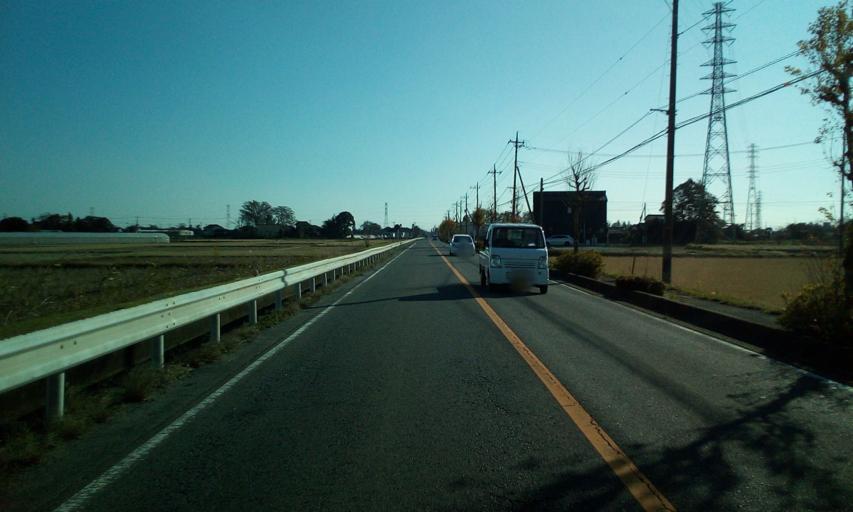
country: JP
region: Saitama
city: Kasukabe
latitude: 36.0151
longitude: 139.7920
